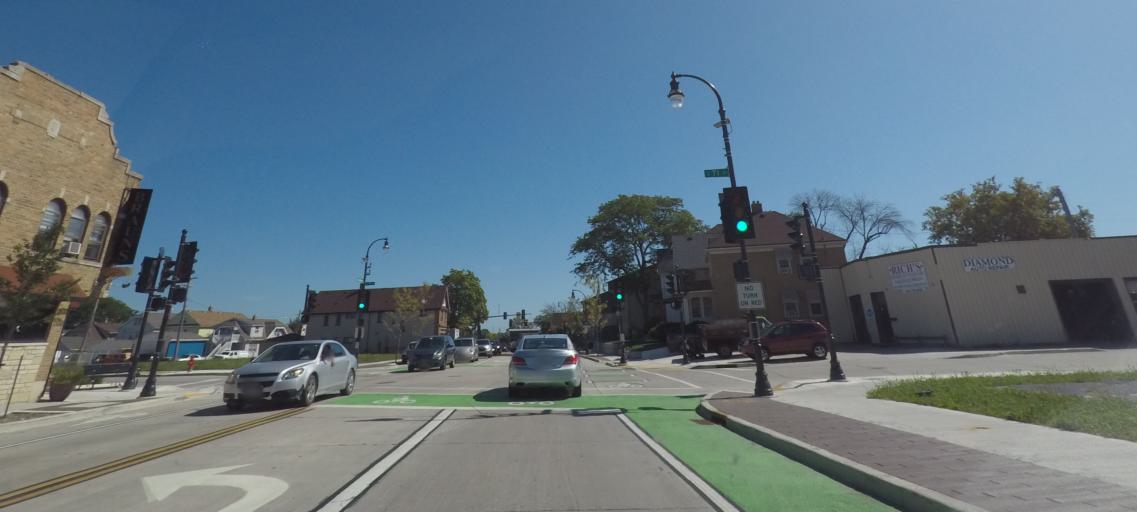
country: US
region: Wisconsin
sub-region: Milwaukee County
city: West Allis
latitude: 43.0128
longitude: -88.0017
